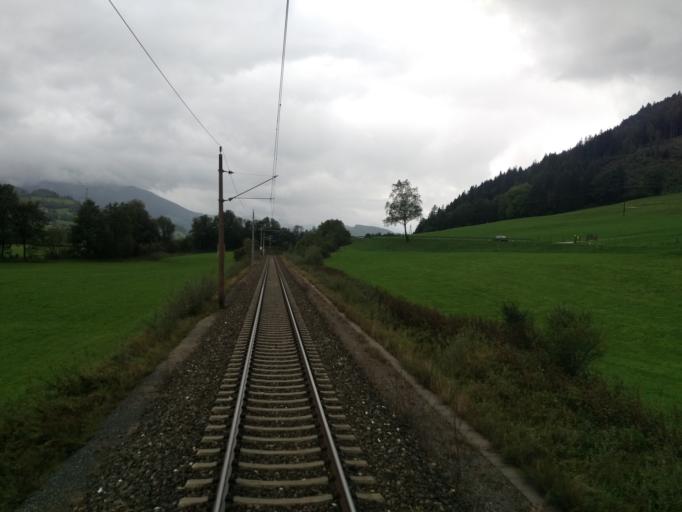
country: AT
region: Styria
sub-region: Politischer Bezirk Liezen
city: Niederoblarn
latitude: 47.5047
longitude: 14.0458
